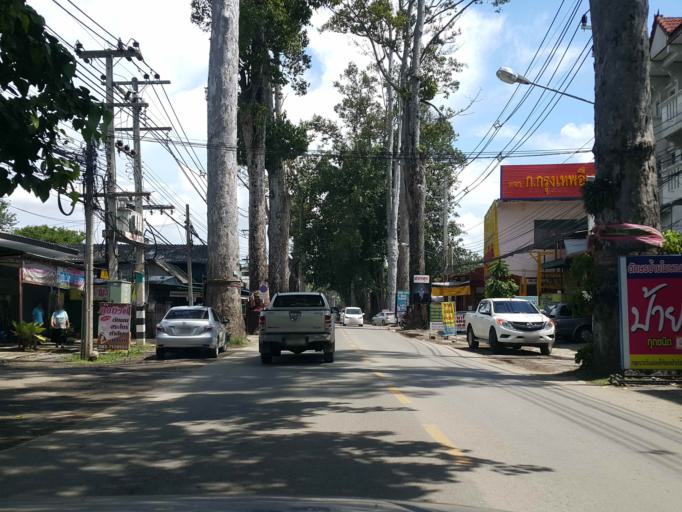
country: TH
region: Chiang Mai
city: Chiang Mai
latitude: 18.7621
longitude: 99.0061
